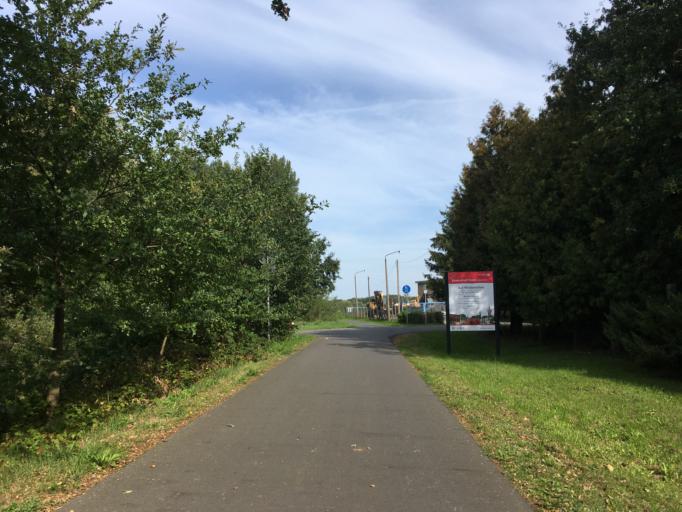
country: DE
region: Brandenburg
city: Forst
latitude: 51.8046
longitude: 14.6028
